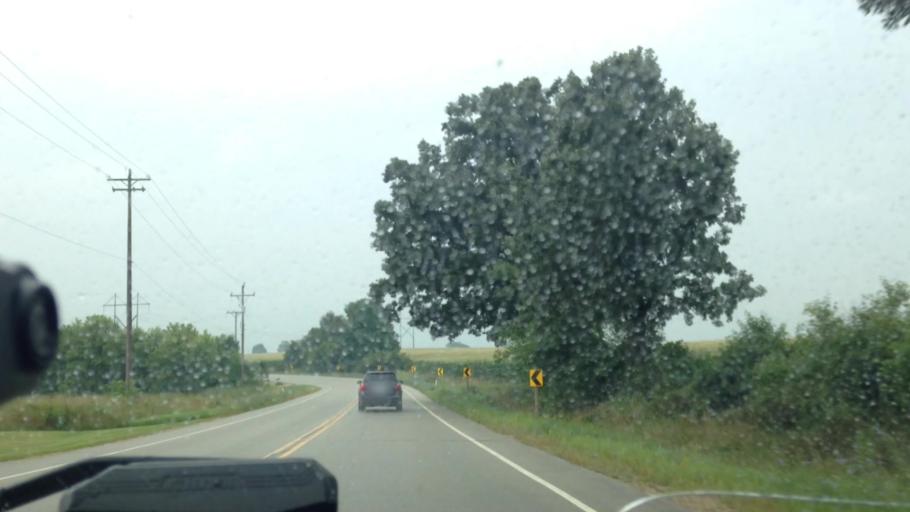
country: US
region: Wisconsin
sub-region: Washington County
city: Hartford
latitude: 43.3917
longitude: -88.3601
